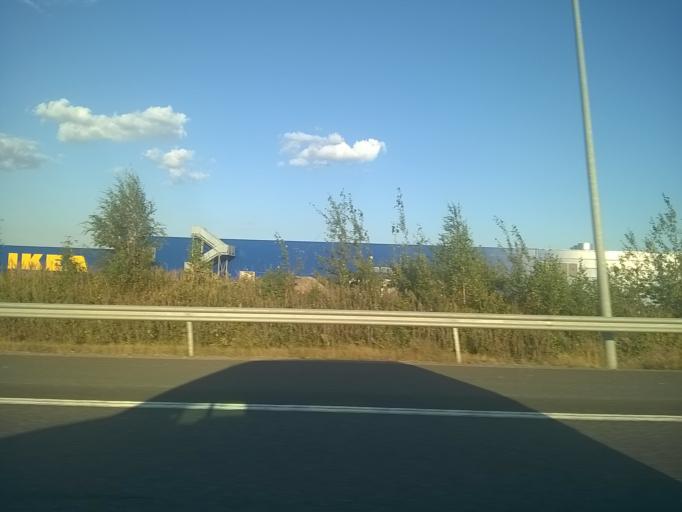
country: FI
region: Pirkanmaa
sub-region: Tampere
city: Tampere
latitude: 61.4541
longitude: 23.7681
